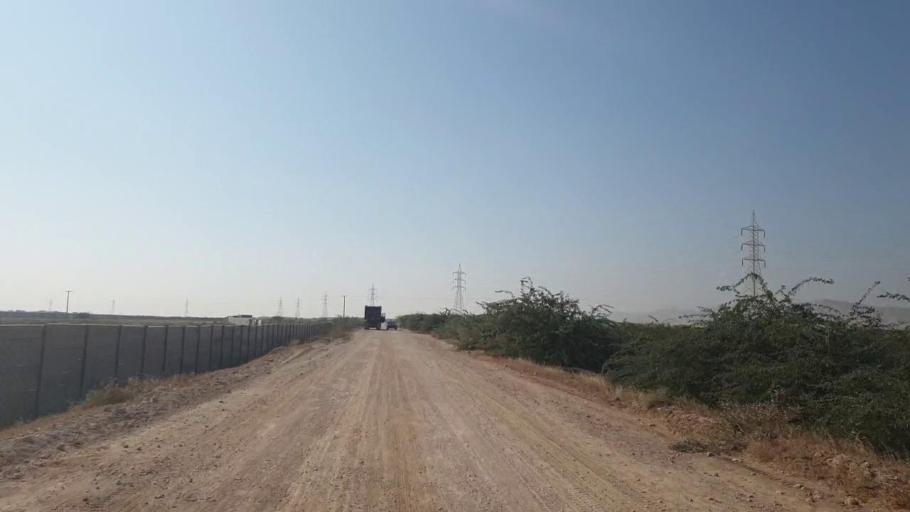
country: PK
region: Sindh
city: Gharo
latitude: 25.1506
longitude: 67.7252
